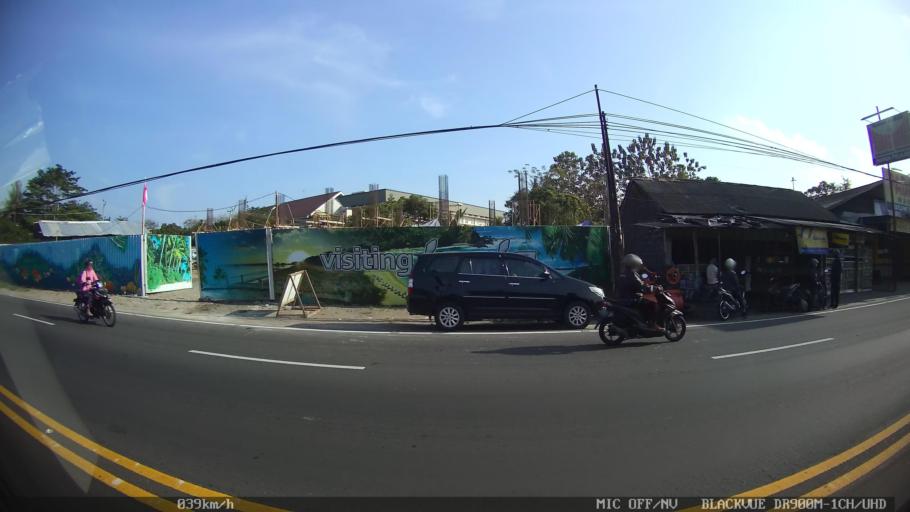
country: ID
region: Daerah Istimewa Yogyakarta
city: Gamping Lor
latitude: -7.8012
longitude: 110.3193
